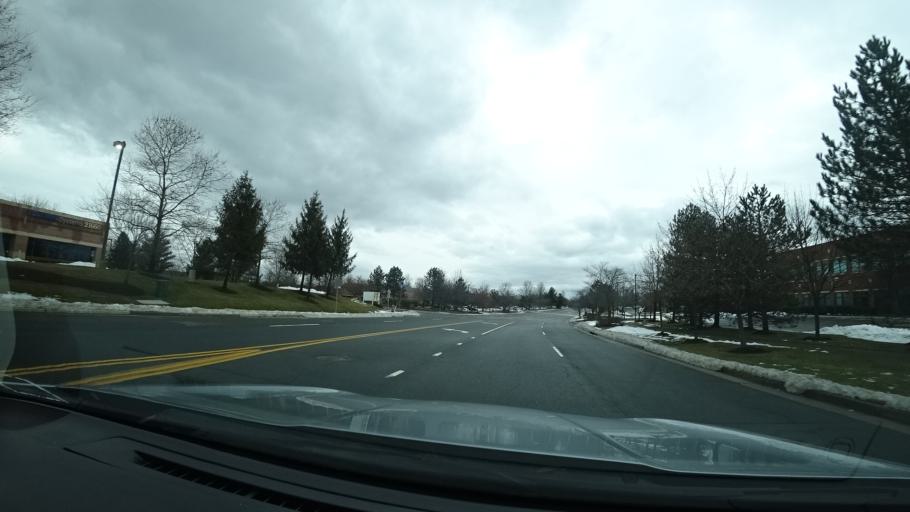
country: US
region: Virginia
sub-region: Loudoun County
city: Dulles Town Center
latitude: 39.0254
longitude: -77.4088
